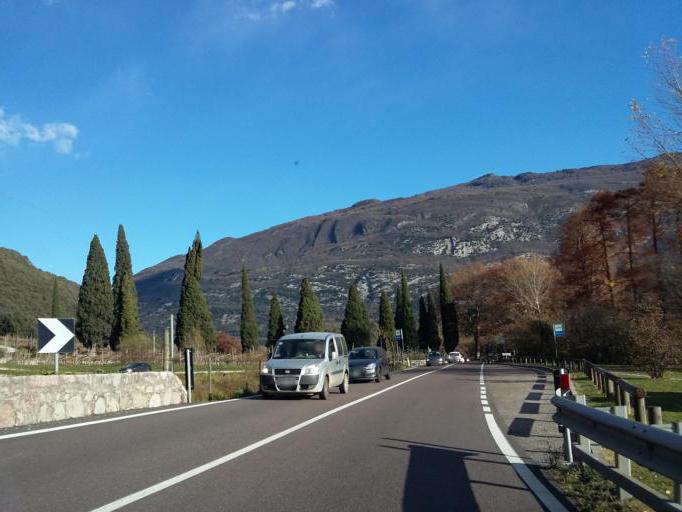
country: IT
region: Trentino-Alto Adige
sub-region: Provincia di Trento
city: Padergnone
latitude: 46.0563
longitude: 10.9647
